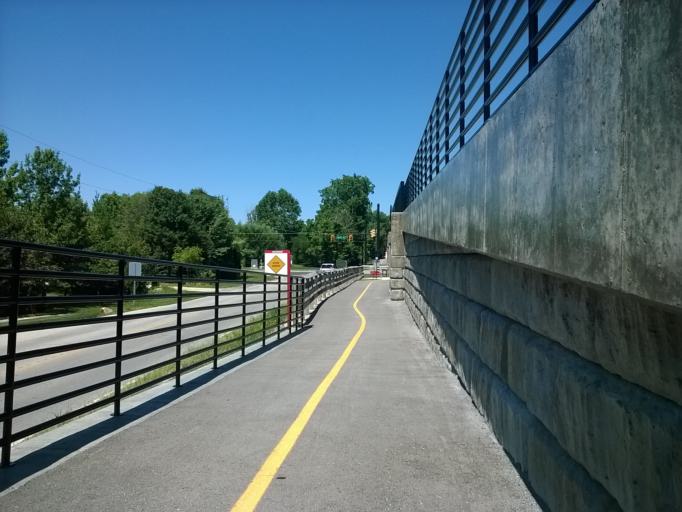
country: US
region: Indiana
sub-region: Hamilton County
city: Carmel
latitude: 39.9991
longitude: -86.1365
